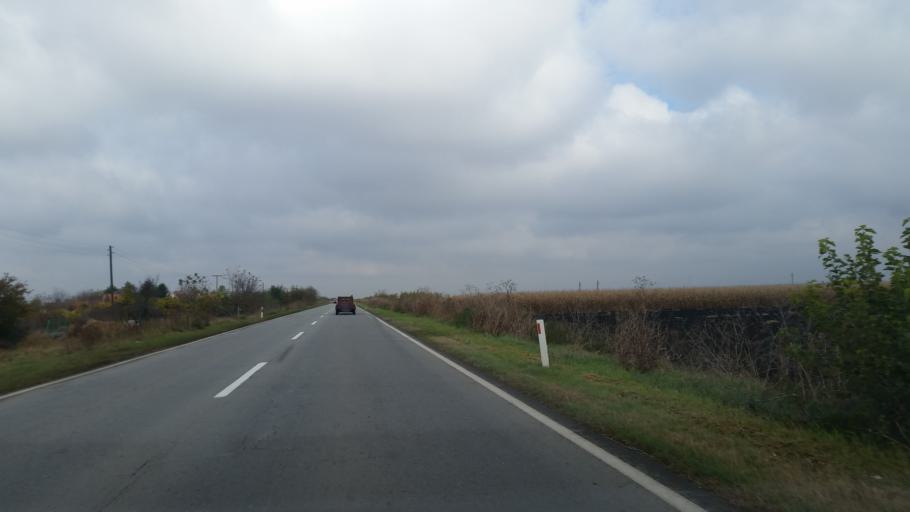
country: RS
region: Autonomna Pokrajina Vojvodina
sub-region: Srednjebanatski Okrug
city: Zrenjanin
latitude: 45.4192
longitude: 20.3716
